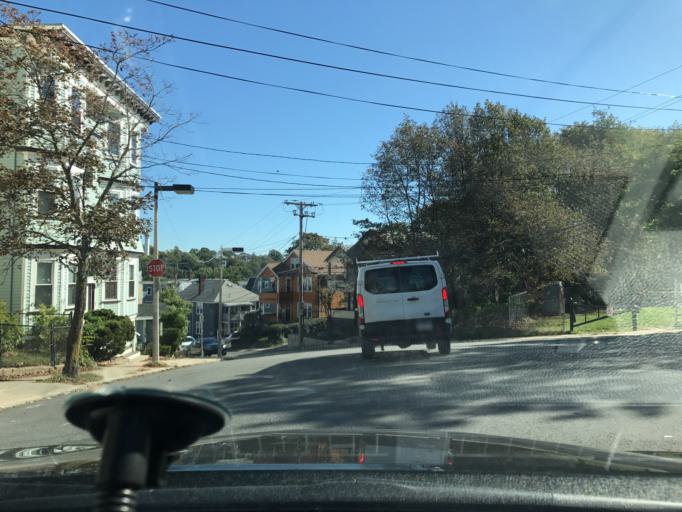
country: US
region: Massachusetts
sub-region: Norfolk County
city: Brookline
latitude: 42.3285
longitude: -71.1004
